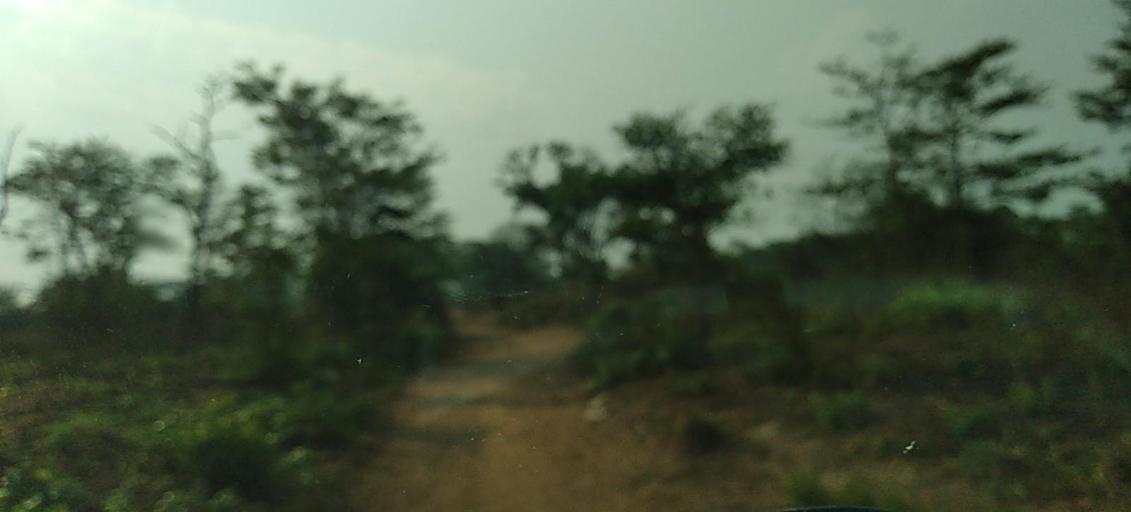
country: ZM
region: North-Western
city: Solwezi
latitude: -12.3567
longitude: 26.5478
